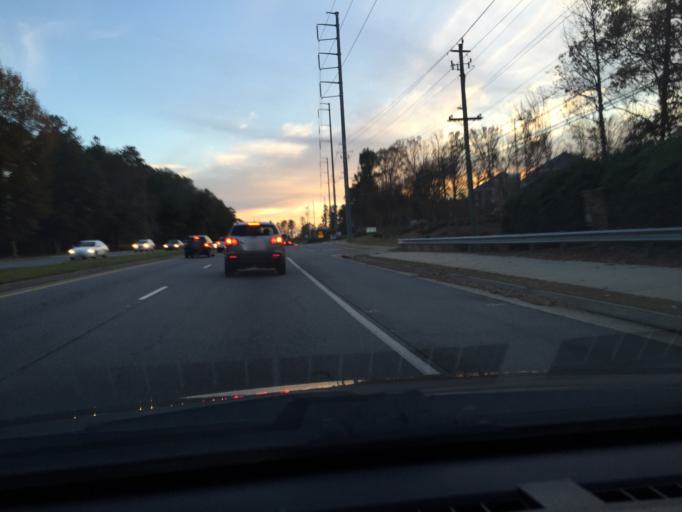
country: US
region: Georgia
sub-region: Fulton County
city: Johns Creek
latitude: 34.0277
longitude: -84.1875
